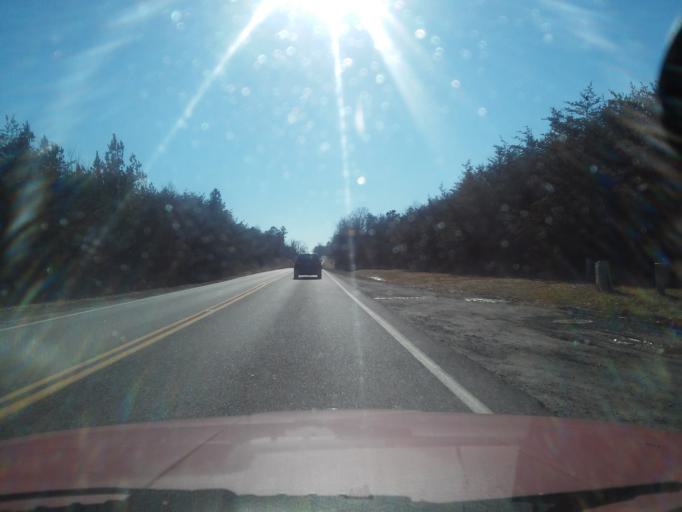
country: US
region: Virginia
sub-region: Orange County
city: Gordonsville
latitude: 37.9932
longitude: -78.1996
